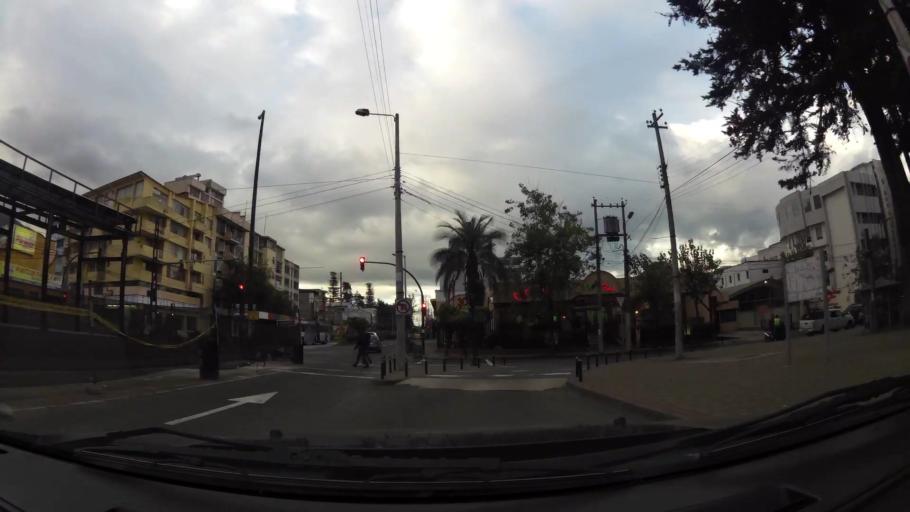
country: EC
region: Pichincha
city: Quito
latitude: -0.2009
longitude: -78.4970
